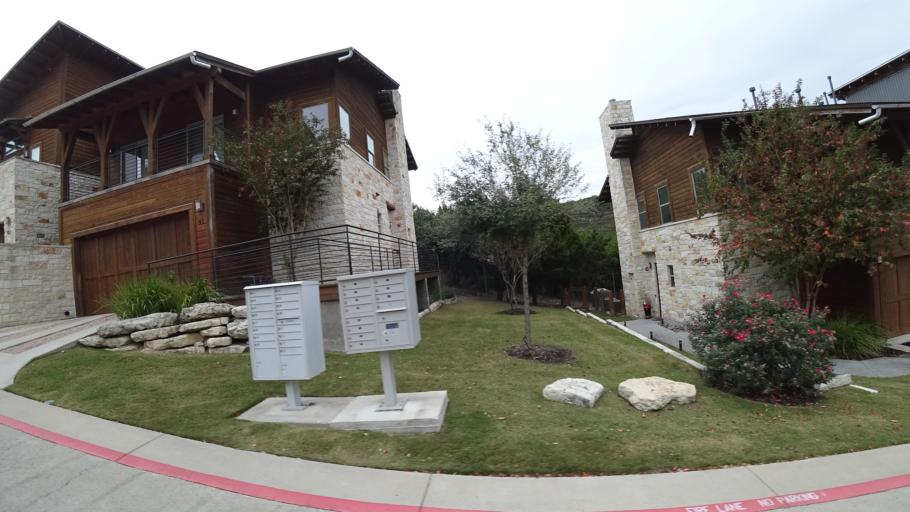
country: US
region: Texas
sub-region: Williamson County
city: Jollyville
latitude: 30.3797
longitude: -97.8047
